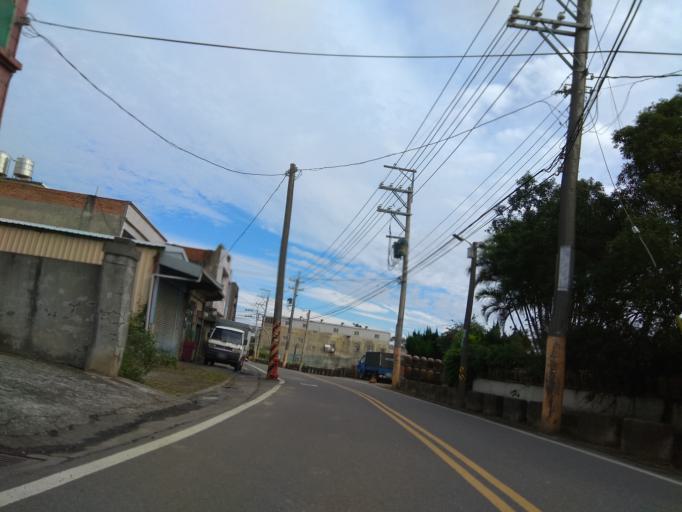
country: TW
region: Taiwan
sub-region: Hsinchu
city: Zhubei
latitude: 24.9565
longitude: 121.1143
